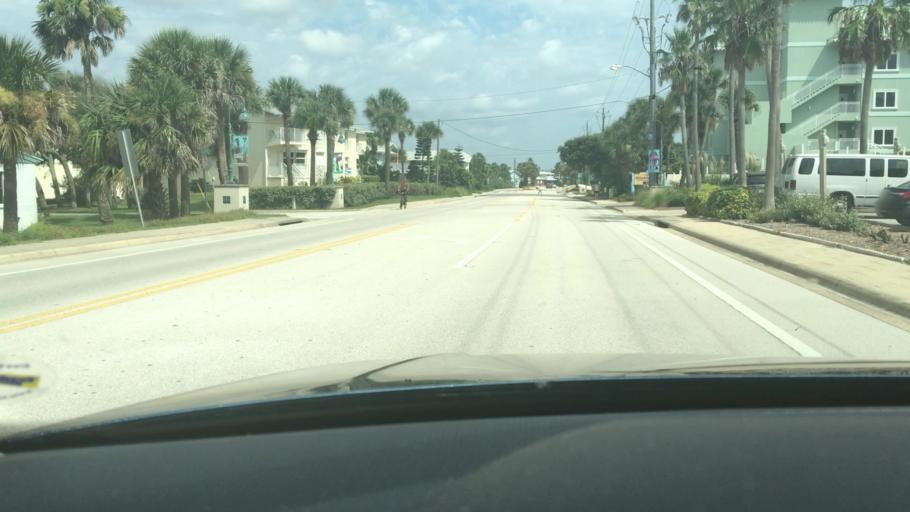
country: US
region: Florida
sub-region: Volusia County
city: New Smyrna Beach
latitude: 29.0350
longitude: -80.8947
